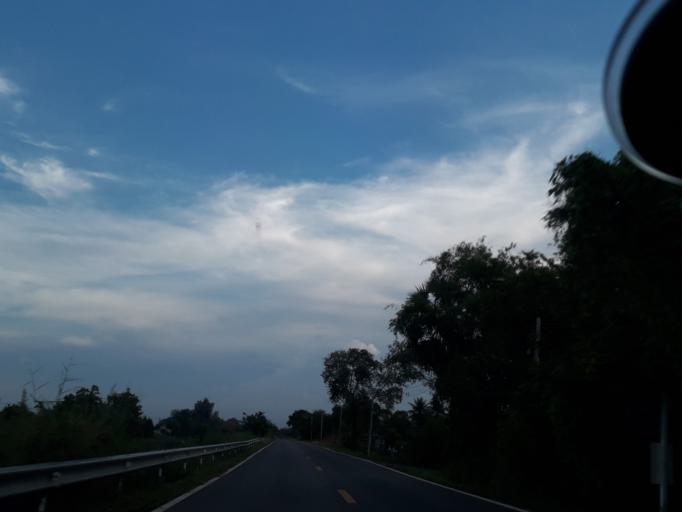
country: TH
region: Sara Buri
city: Nong Khae
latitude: 14.2885
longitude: 100.8911
